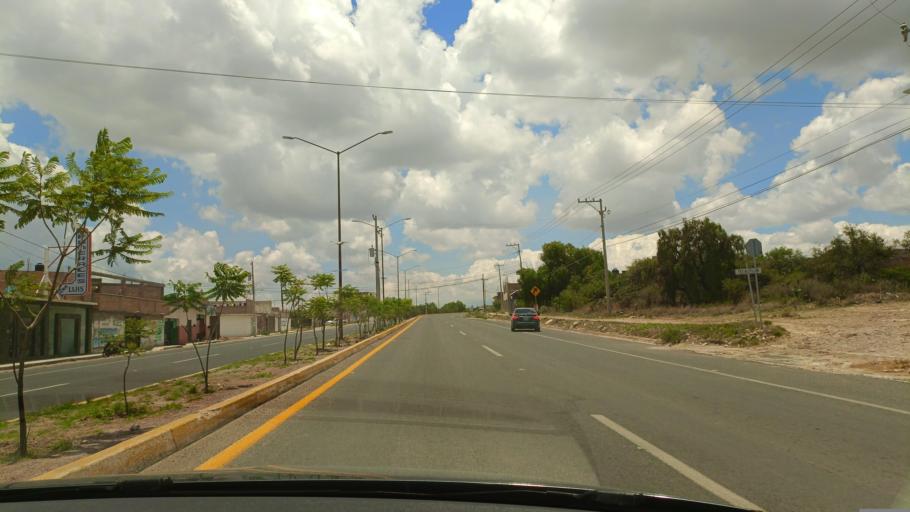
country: MX
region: Guerrero
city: San Luis de la Paz
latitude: 21.2822
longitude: -100.5030
